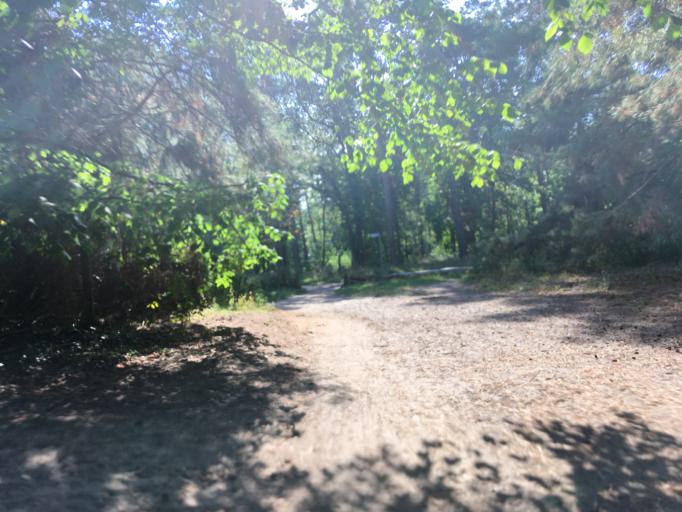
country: DE
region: Berlin
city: Friedrichshagen
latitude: 52.4708
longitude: 13.6208
